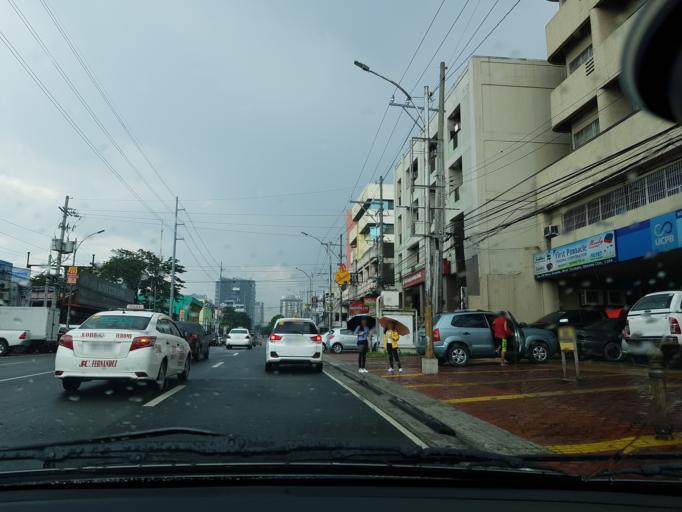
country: PH
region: Calabarzon
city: Del Monte
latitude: 14.6438
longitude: 121.0274
